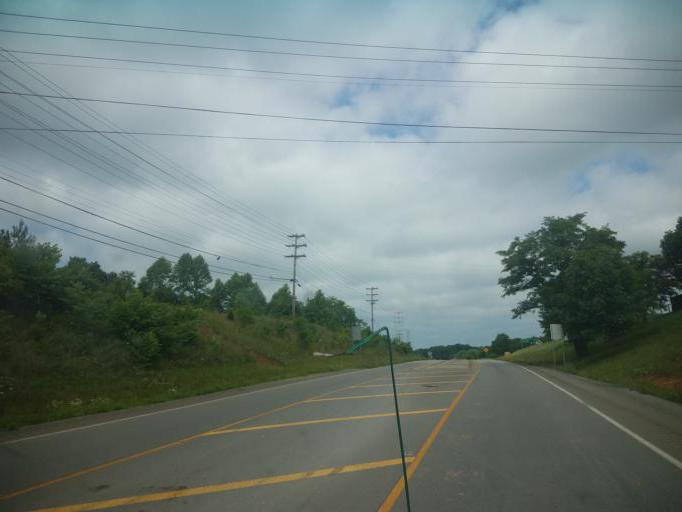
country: US
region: Kentucky
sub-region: Metcalfe County
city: Edmonton
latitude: 36.8777
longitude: -85.6664
